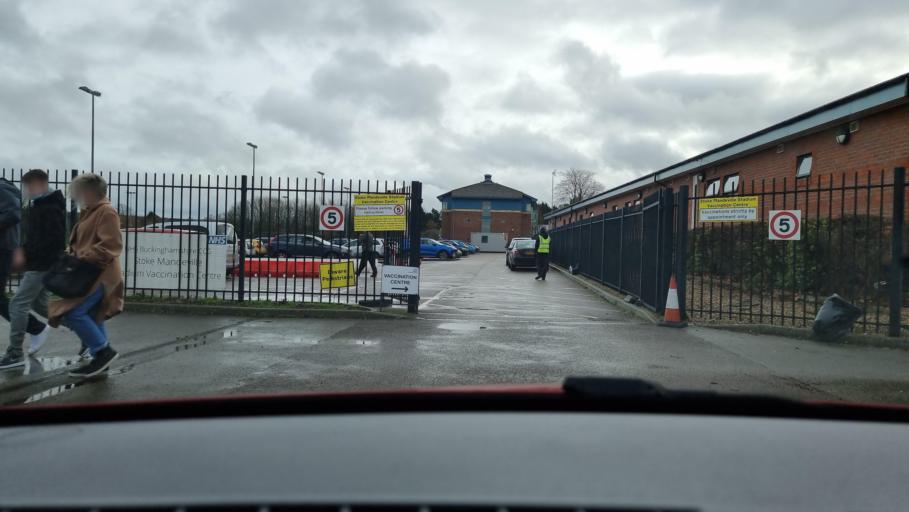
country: GB
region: England
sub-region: Buckinghamshire
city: Aylesbury
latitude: 51.8001
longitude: -0.8007
